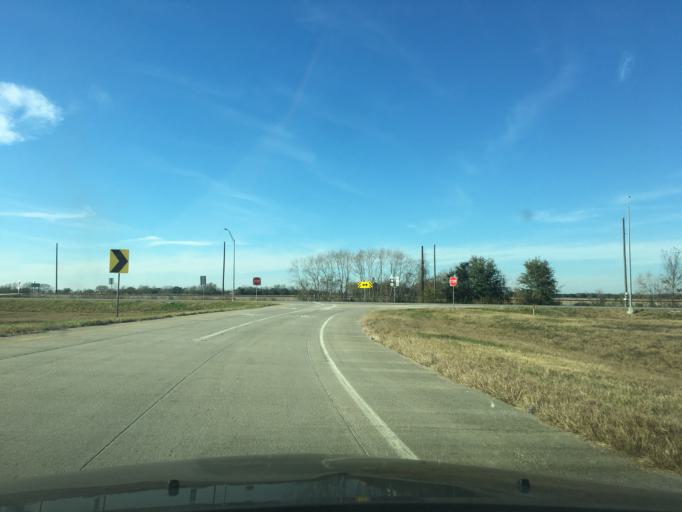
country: US
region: Texas
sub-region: Fort Bend County
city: Pleak
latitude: 29.4859
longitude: -95.9353
